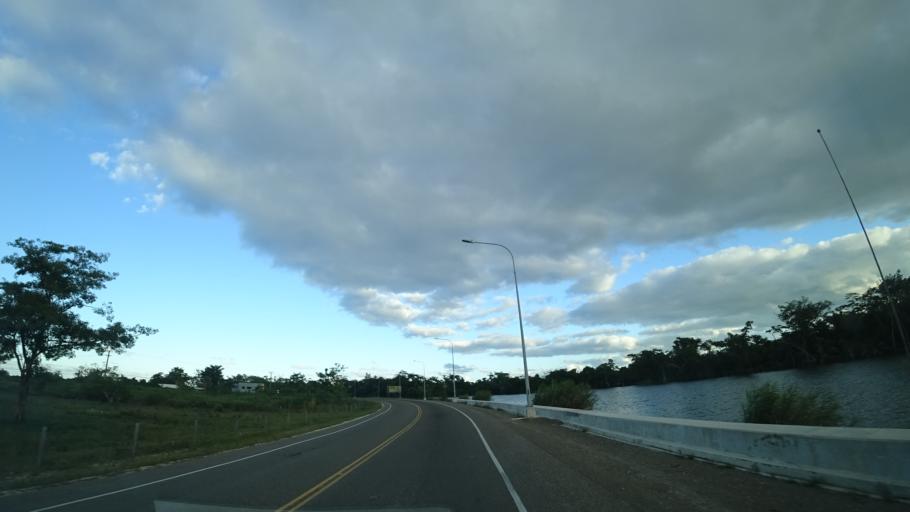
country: BZ
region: Belize
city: Belize City
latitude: 17.5428
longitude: -88.2636
